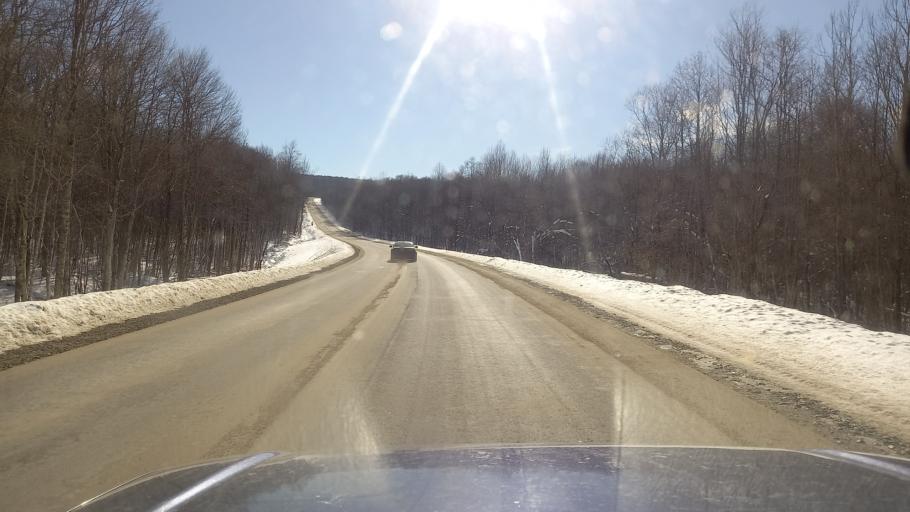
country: RU
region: Adygeya
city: Kamennomostskiy
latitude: 44.2131
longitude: 40.0766
